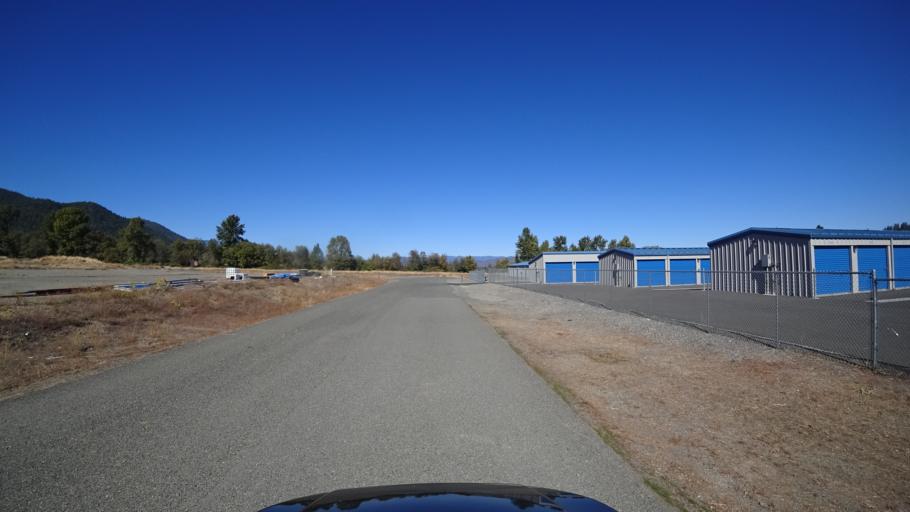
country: US
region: California
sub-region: Siskiyou County
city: Yreka
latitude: 41.4636
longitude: -122.8908
